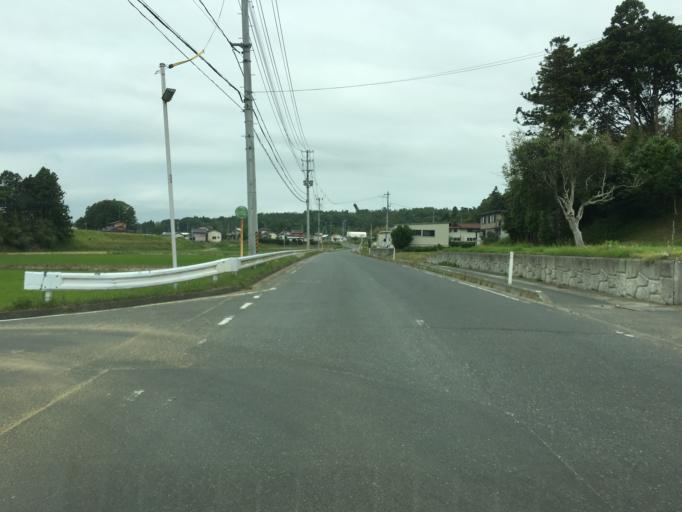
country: JP
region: Fukushima
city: Namie
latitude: 37.6636
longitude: 141.0111
